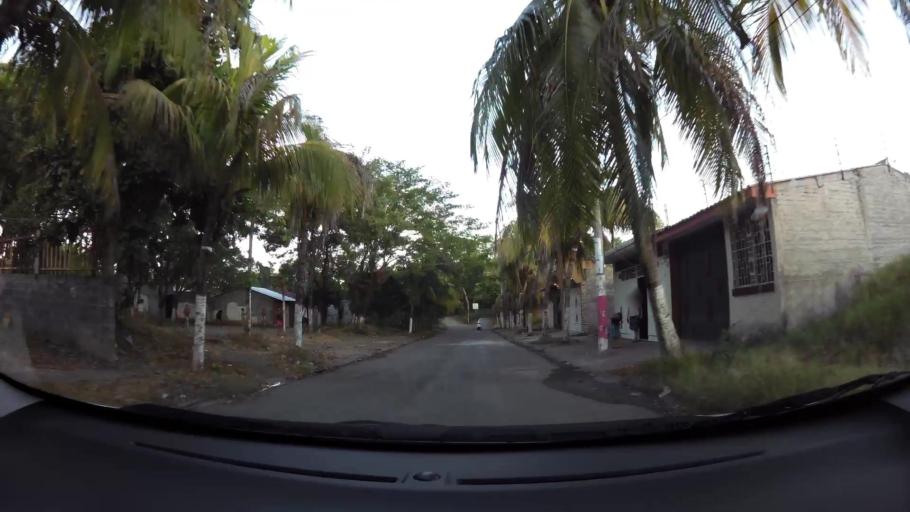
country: SV
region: San Miguel
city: San Miguel
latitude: 13.4790
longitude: -88.1572
